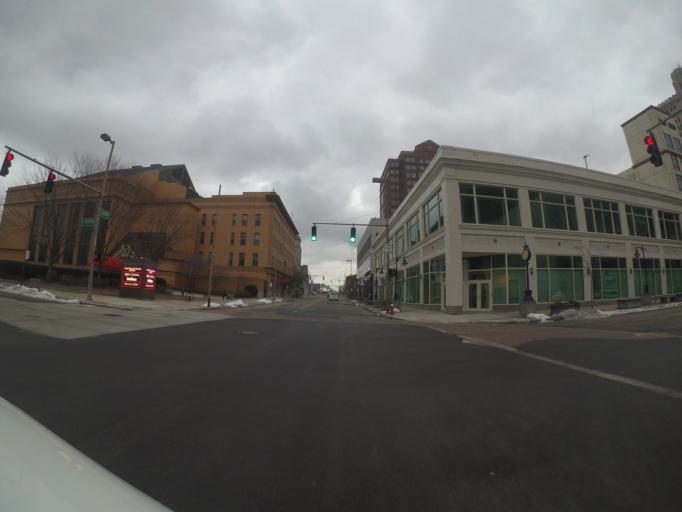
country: US
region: Ohio
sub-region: Lucas County
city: Toledo
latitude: 41.6531
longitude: -83.5349
